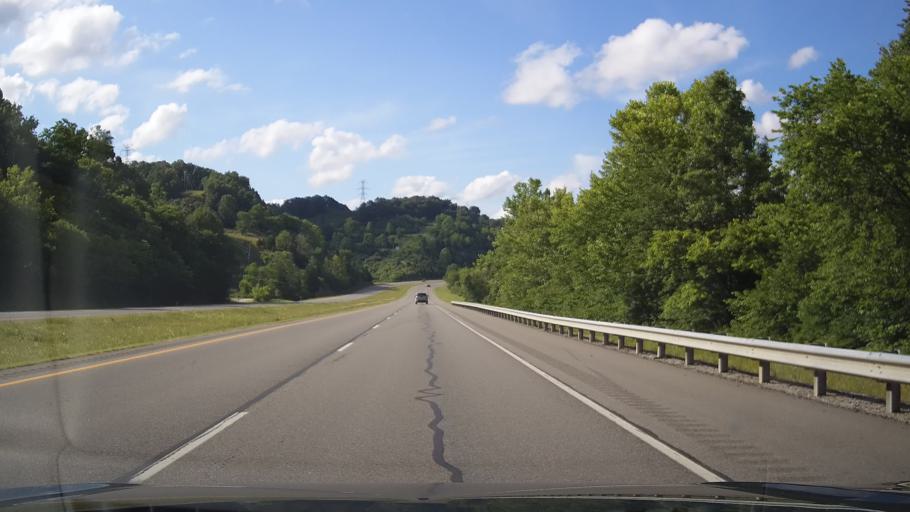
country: US
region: Kentucky
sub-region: Lawrence County
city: Louisa
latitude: 38.2300
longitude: -82.6125
